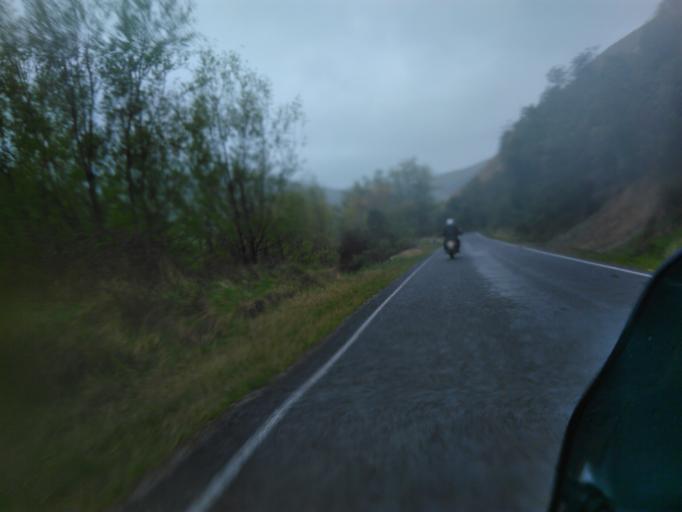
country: NZ
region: Gisborne
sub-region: Gisborne District
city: Gisborne
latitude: -38.6724
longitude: 177.7183
